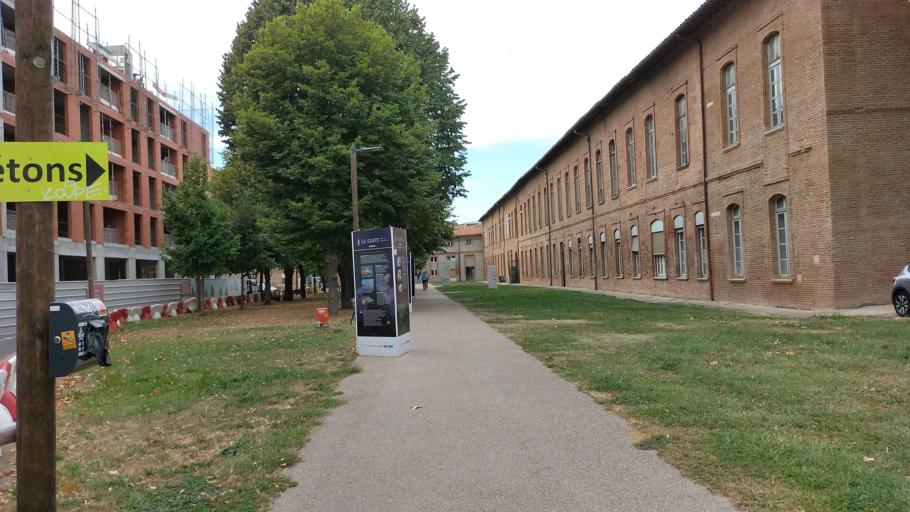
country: FR
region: Midi-Pyrenees
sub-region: Departement de la Haute-Garonne
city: Toulouse
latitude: 43.6001
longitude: 1.4328
